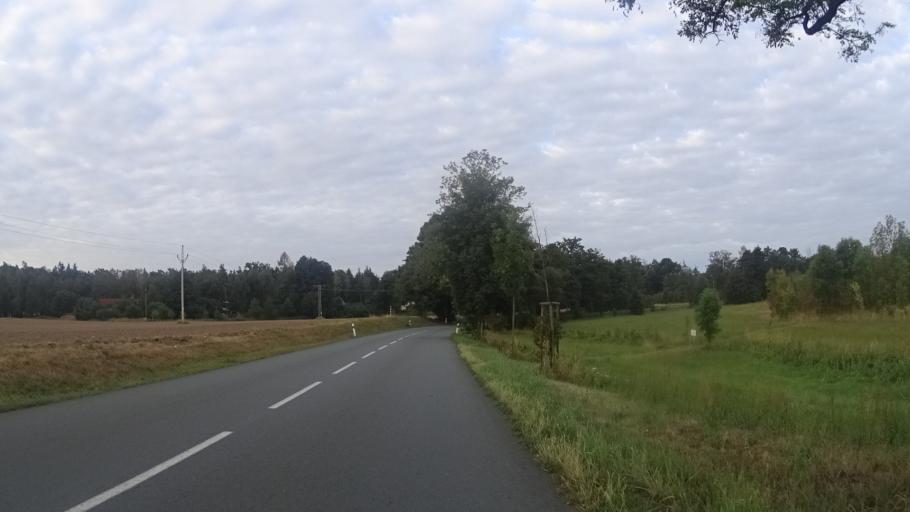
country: CZ
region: Kralovehradecky
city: Cernilov
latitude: 50.2080
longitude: 15.8998
